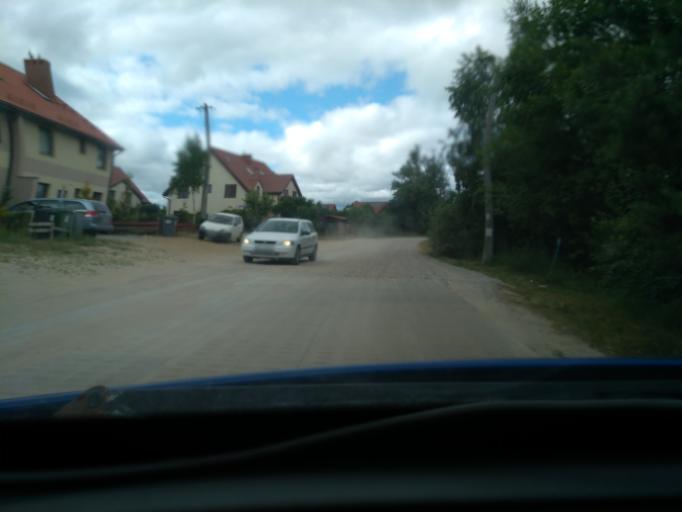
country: PL
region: Pomeranian Voivodeship
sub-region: Powiat kartuski
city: Banino
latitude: 54.4005
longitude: 18.3977
